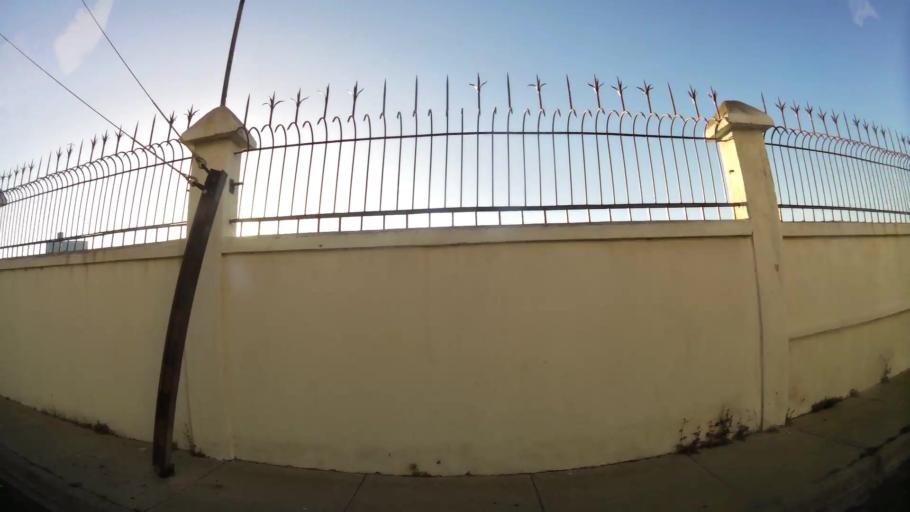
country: CL
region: Valparaiso
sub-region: Provincia de Valparaiso
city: Vina del Mar
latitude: -33.0213
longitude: -71.5657
